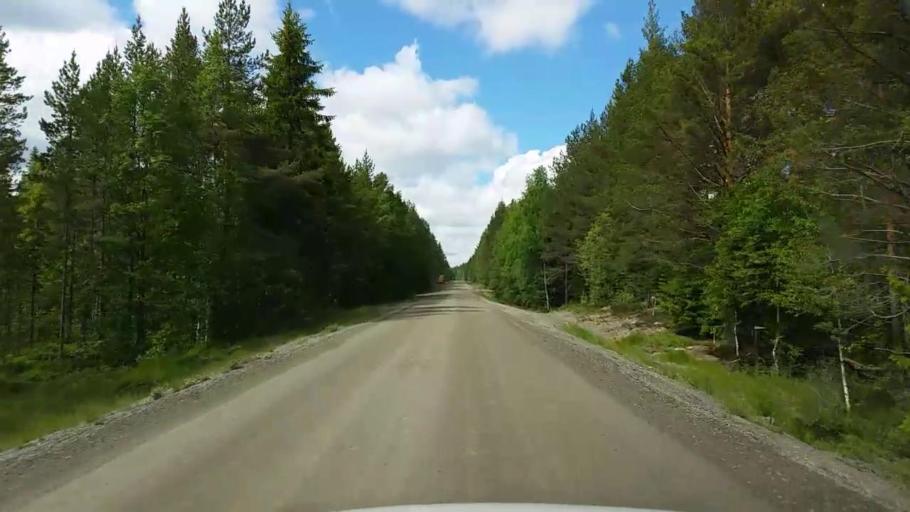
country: SE
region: Gaevleborg
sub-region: Bollnas Kommun
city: Vittsjo
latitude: 61.0355
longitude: 16.3633
